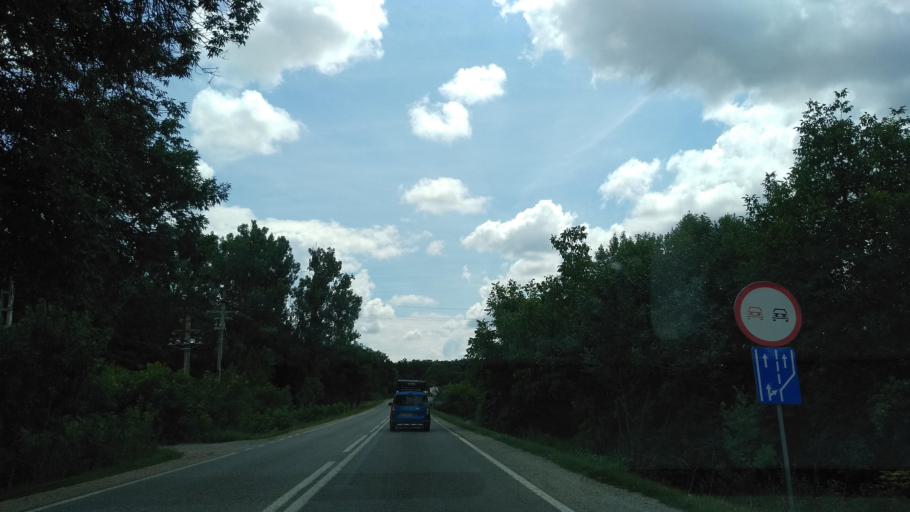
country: RO
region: Gorj
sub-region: Comuna Balanesti
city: Balanesti
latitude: 45.0344
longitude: 23.3900
